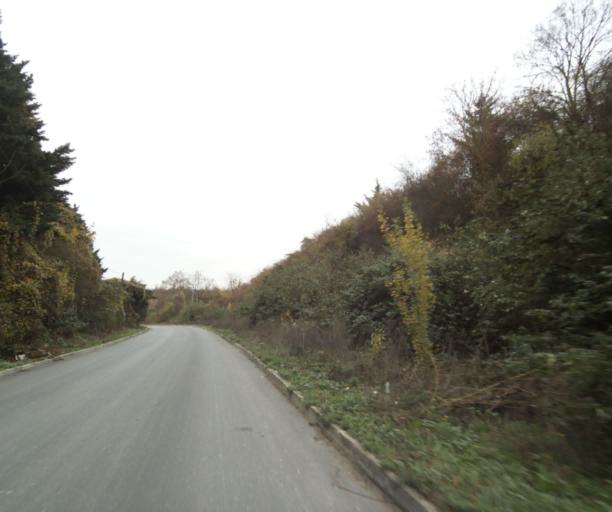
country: FR
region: Ile-de-France
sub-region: Departement de Seine-Saint-Denis
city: Le Blanc-Mesnil
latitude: 48.9642
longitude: 2.4654
